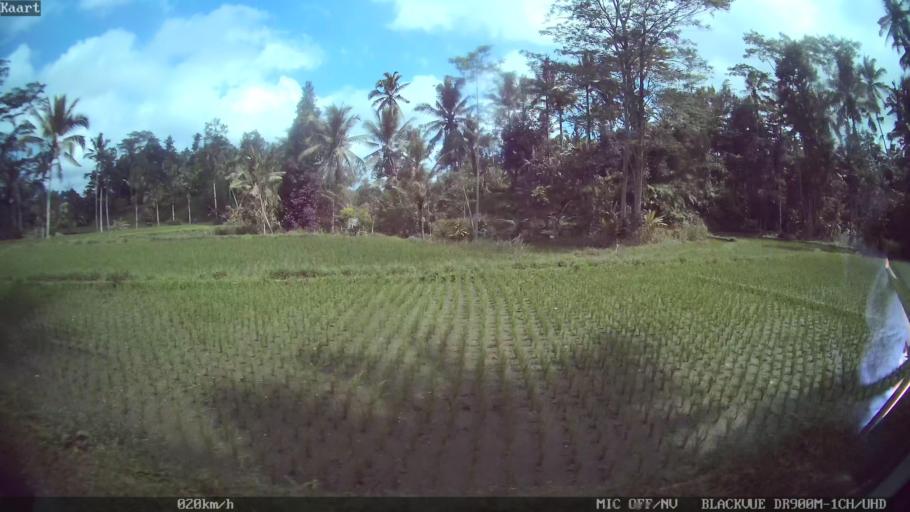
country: ID
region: Bali
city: Banjar Petak
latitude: -8.4494
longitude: 115.3252
